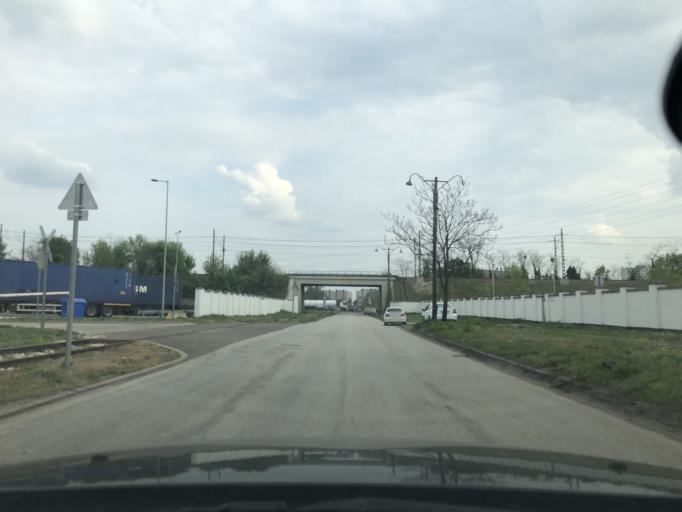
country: HU
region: Budapest
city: Budapest XXI. keruelet
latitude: 47.4408
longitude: 19.0693
